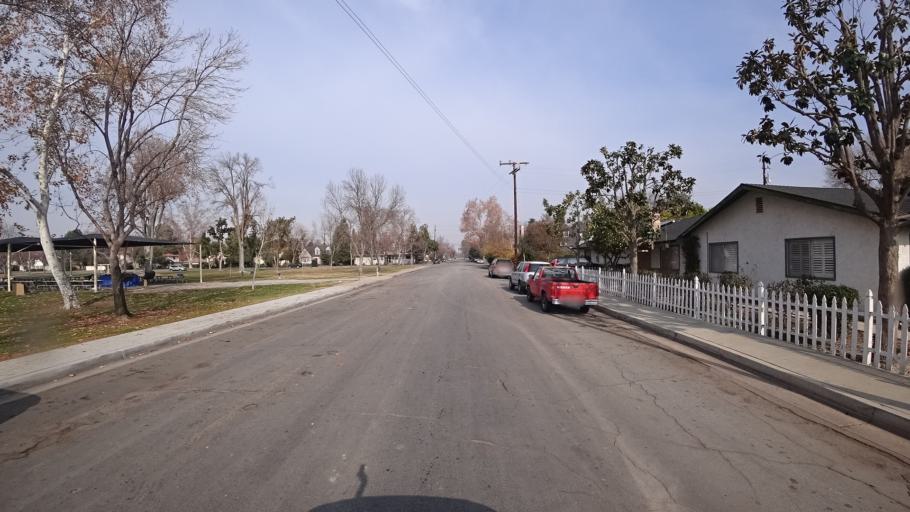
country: US
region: California
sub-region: Kern County
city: Bakersfield
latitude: 35.3746
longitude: -119.0340
